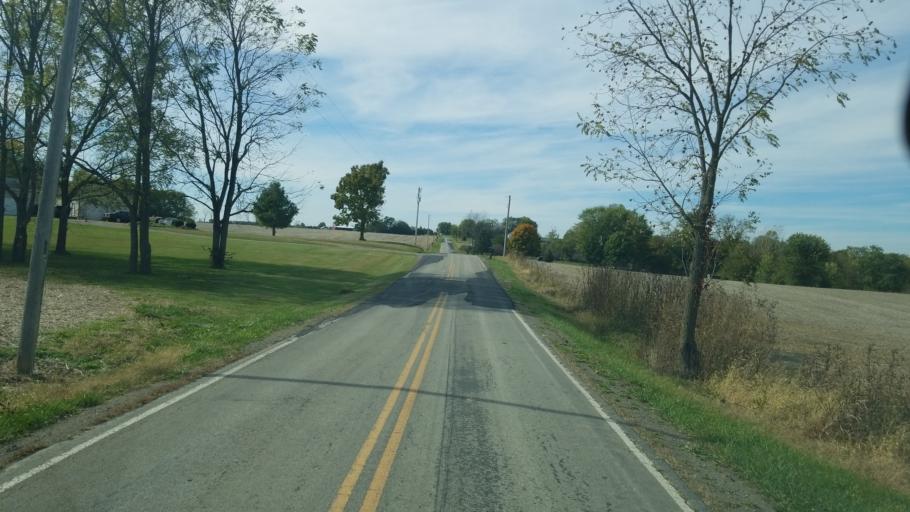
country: US
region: Ohio
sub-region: Highland County
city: Leesburg
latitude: 39.3298
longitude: -83.4925
